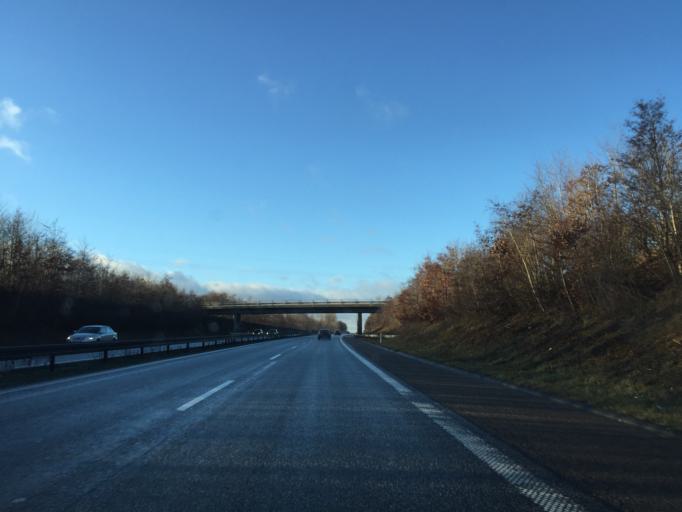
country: DK
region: Zealand
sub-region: Ringsted Kommune
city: Ringsted
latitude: 55.4545
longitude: 11.7331
